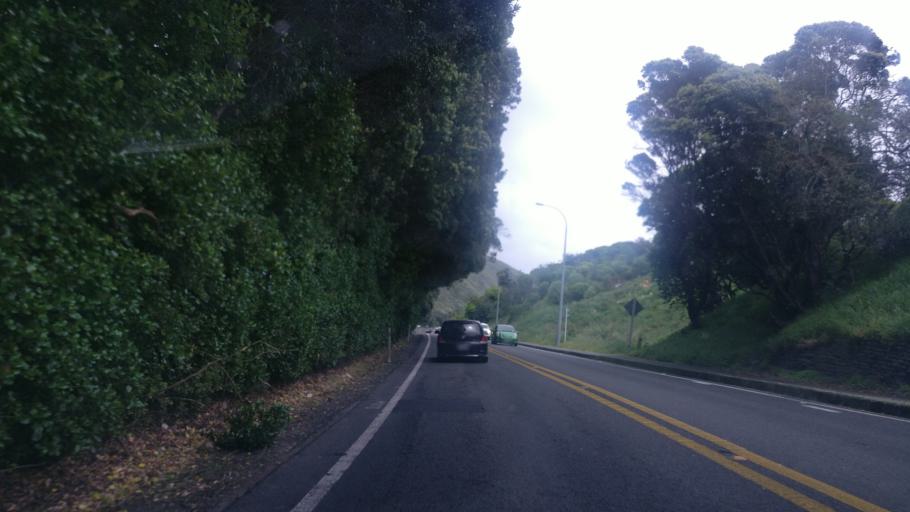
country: NZ
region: Wellington
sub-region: Kapiti Coast District
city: Paraparaumu
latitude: -40.9942
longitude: 174.9462
